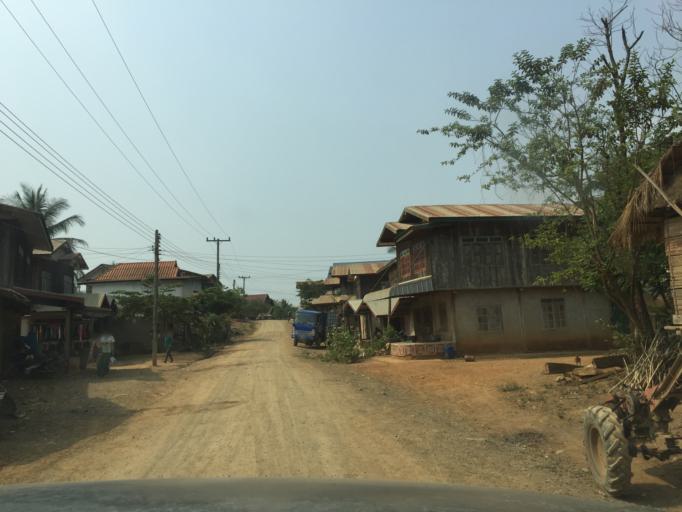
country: TH
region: Uttaradit
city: Ban Khok
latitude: 17.9499
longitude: 101.2836
